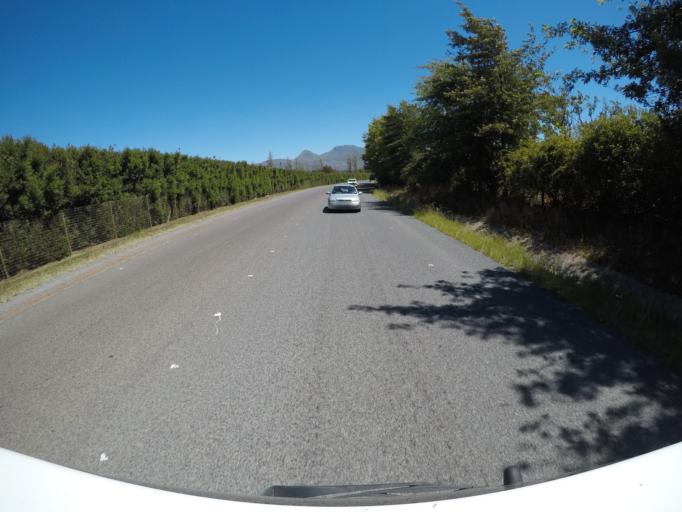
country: ZA
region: Western Cape
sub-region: Overberg District Municipality
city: Grabouw
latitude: -34.1776
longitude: 19.0351
